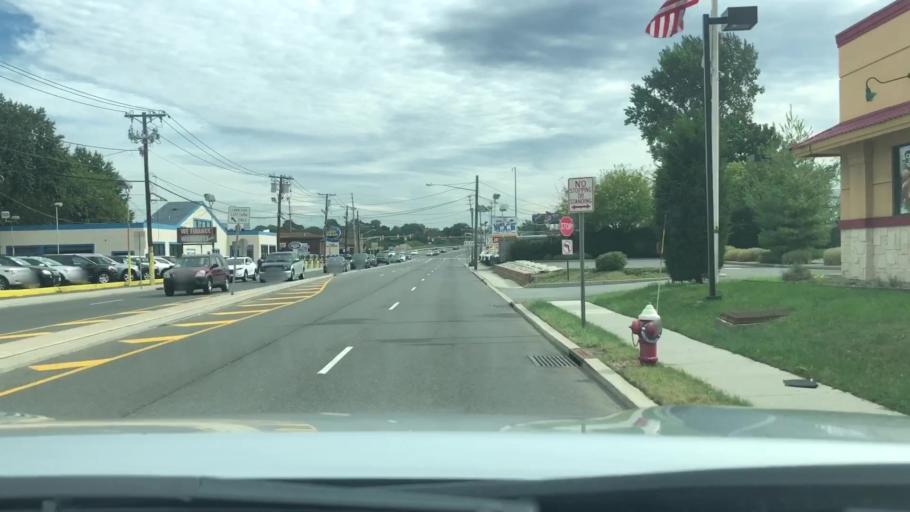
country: US
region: New Jersey
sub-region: Bergen County
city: Little Ferry
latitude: 40.8534
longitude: -74.0366
